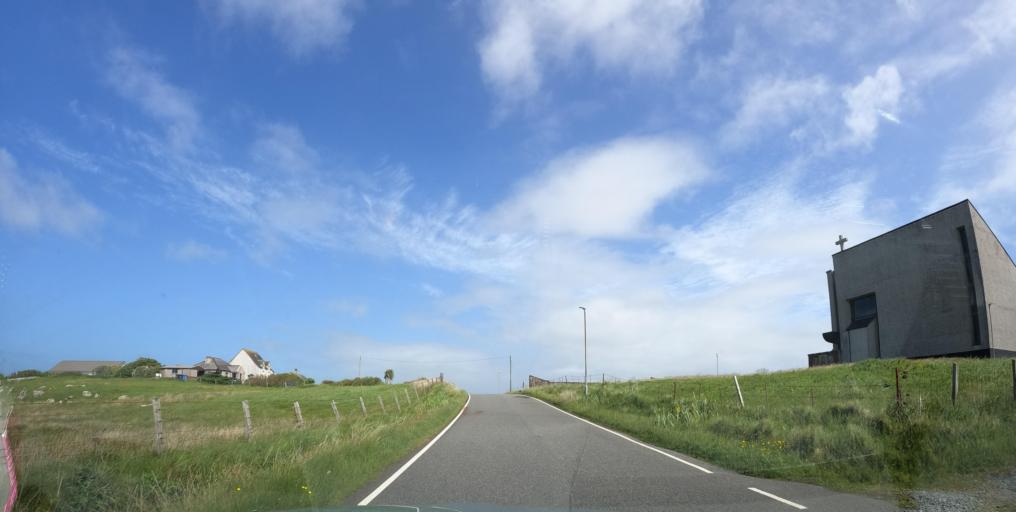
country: GB
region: Scotland
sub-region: Eilean Siar
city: Isle of South Uist
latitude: 57.1240
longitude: -7.3594
